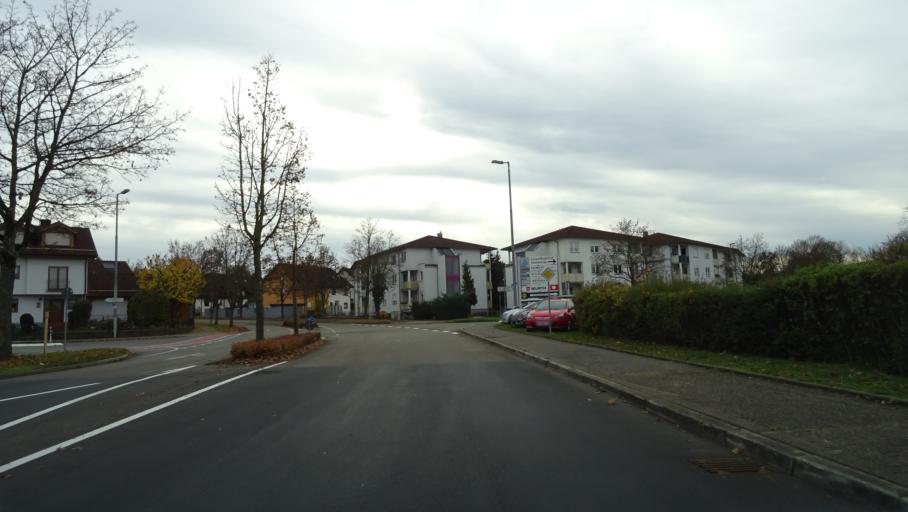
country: DE
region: Baden-Wuerttemberg
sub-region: Karlsruhe Region
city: Neckarzimmern
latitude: 49.3389
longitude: 9.1214
